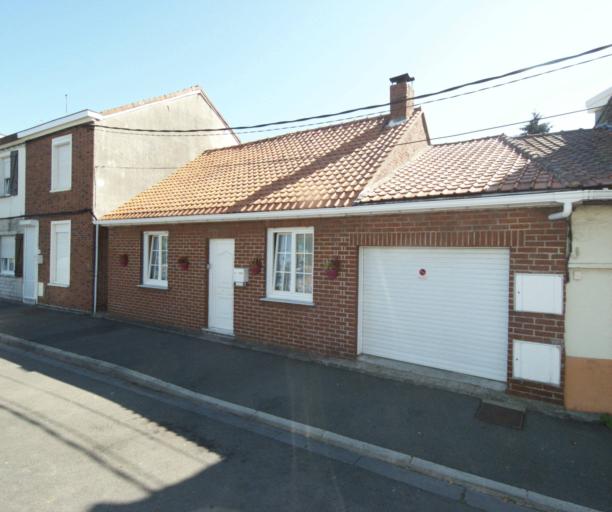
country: FR
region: Nord-Pas-de-Calais
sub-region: Departement du Nord
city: Wattrelos
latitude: 50.7109
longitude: 3.2023
